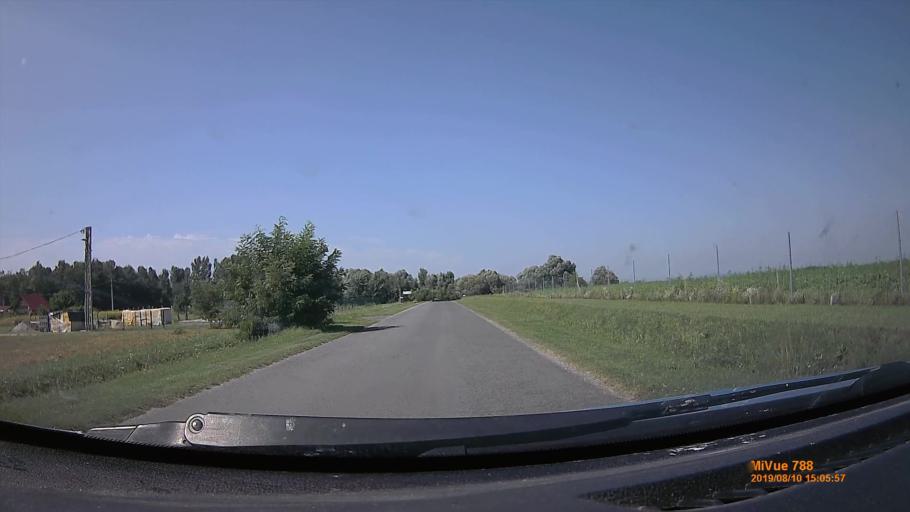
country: HU
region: Somogy
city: Fonyod
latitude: 46.6820
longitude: 17.5643
